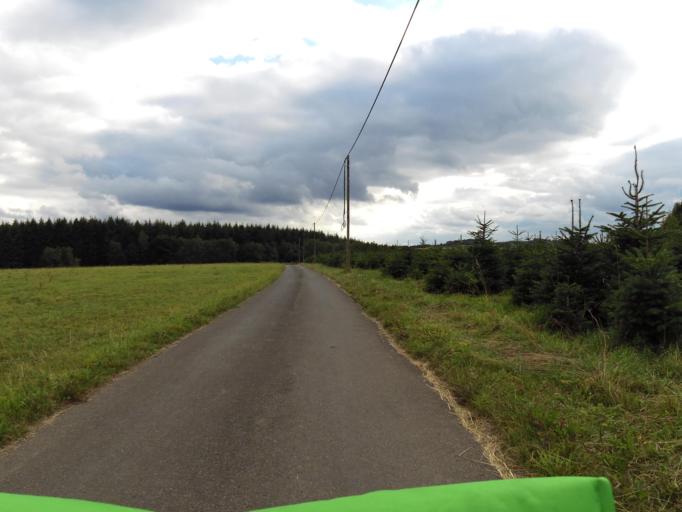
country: BE
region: Wallonia
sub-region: Province de Namur
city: Bievre
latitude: 49.8832
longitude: 4.9984
